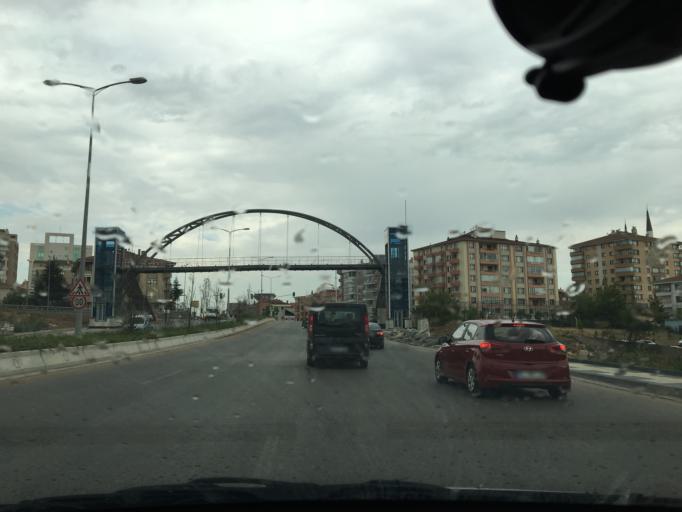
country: TR
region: Ankara
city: Ankara
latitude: 39.8860
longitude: 32.8254
